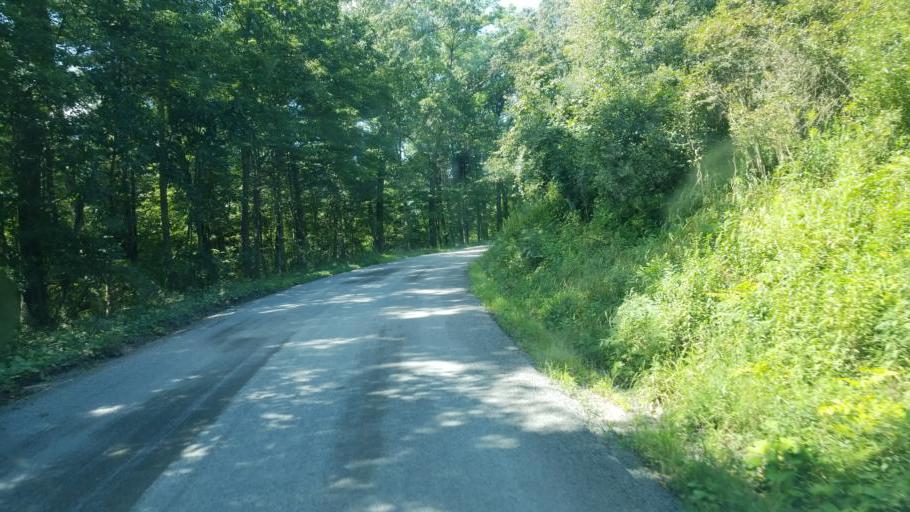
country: US
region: Pennsylvania
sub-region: Clarion County
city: Clarion
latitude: 41.1688
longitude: -79.4346
